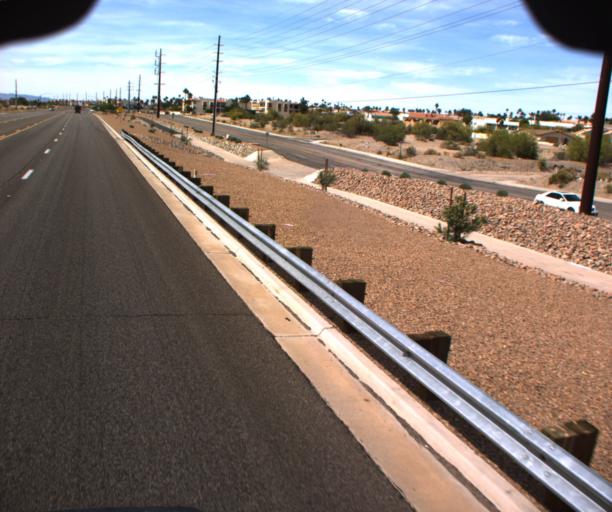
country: US
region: Arizona
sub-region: Mohave County
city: Lake Havasu City
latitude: 34.4597
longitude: -114.3318
